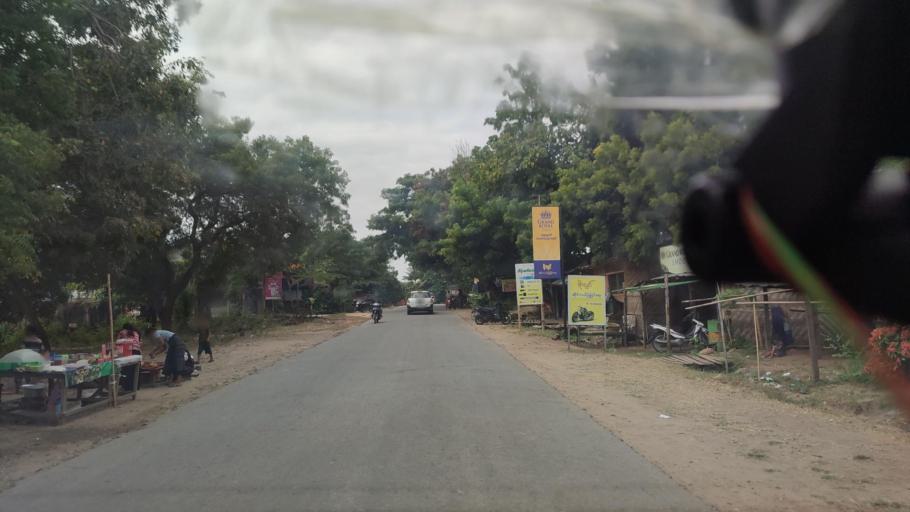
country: MM
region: Mandalay
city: Pyinmana
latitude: 19.7647
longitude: 96.3180
